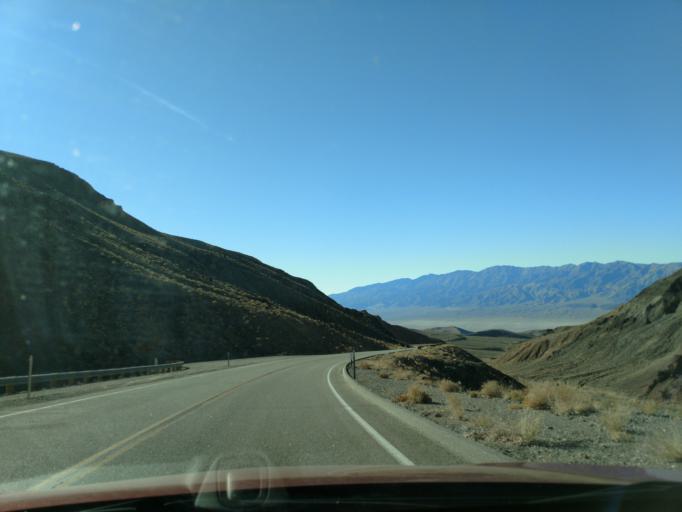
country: US
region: California
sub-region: San Bernardino County
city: Searles Valley
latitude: 36.3645
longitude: -117.2862
